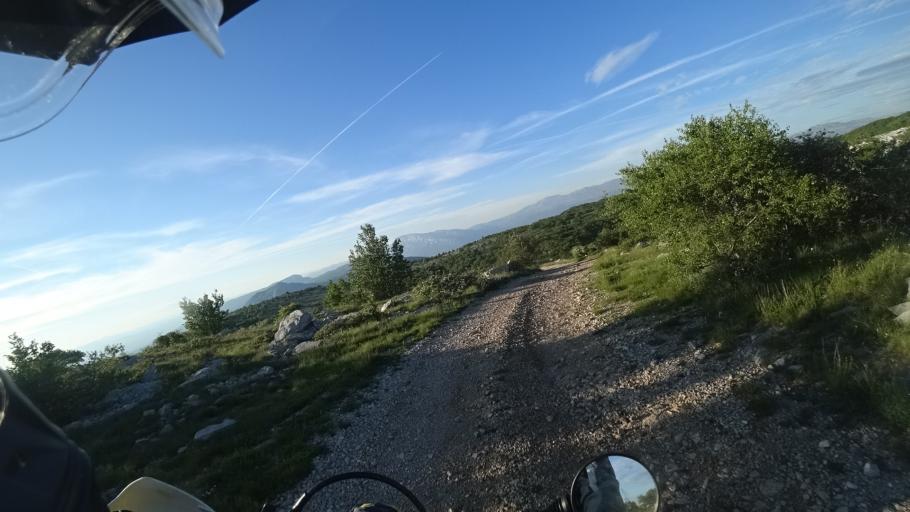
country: HR
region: Sibensko-Kniniska
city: Drnis
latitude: 43.8711
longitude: 16.3577
